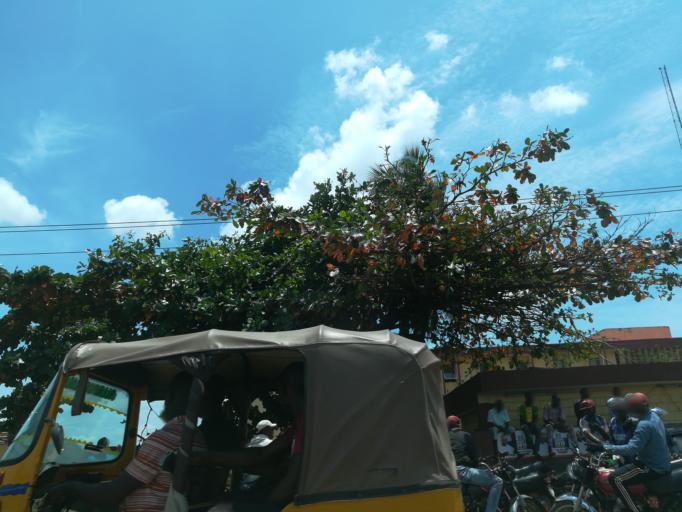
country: NG
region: Lagos
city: Ikorodu
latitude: 6.6092
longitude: 3.4990
